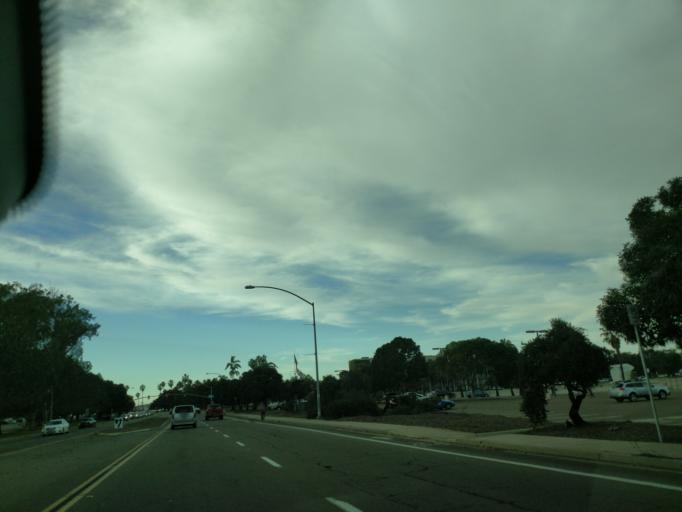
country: US
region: California
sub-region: San Diego County
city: La Jolla
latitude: 32.7699
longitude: -117.2451
